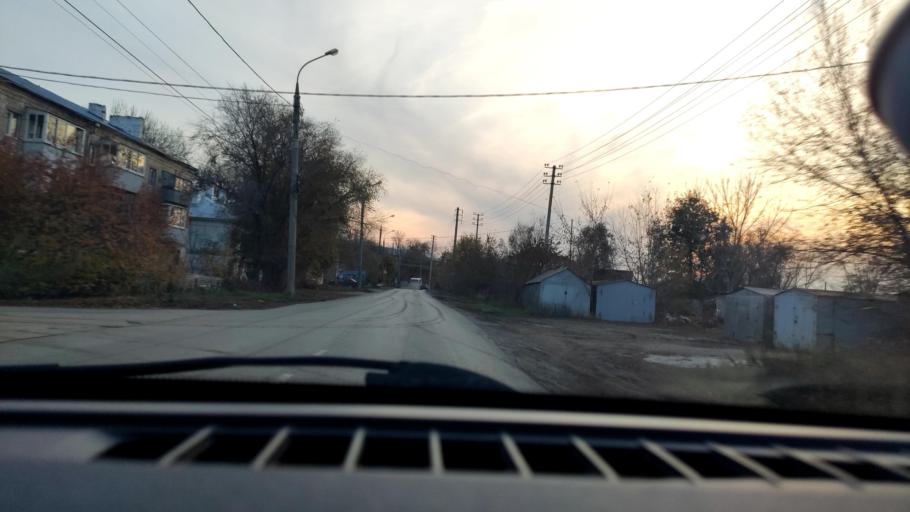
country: RU
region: Samara
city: Samara
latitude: 53.1386
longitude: 50.1274
